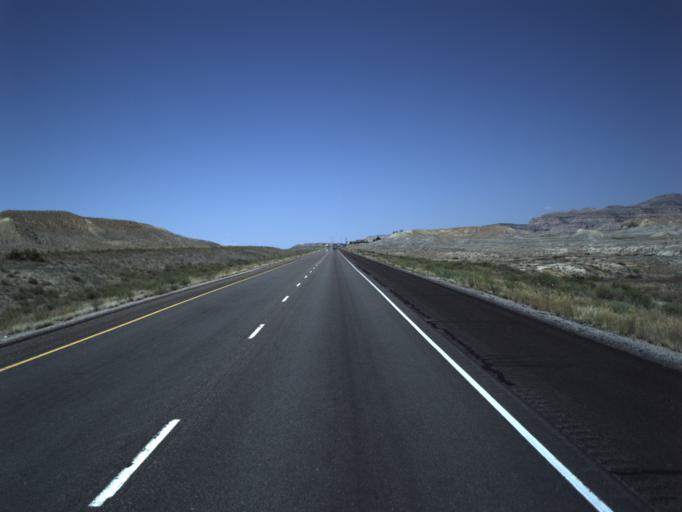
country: US
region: Utah
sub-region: Grand County
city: Moab
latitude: 38.9486
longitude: -109.6677
